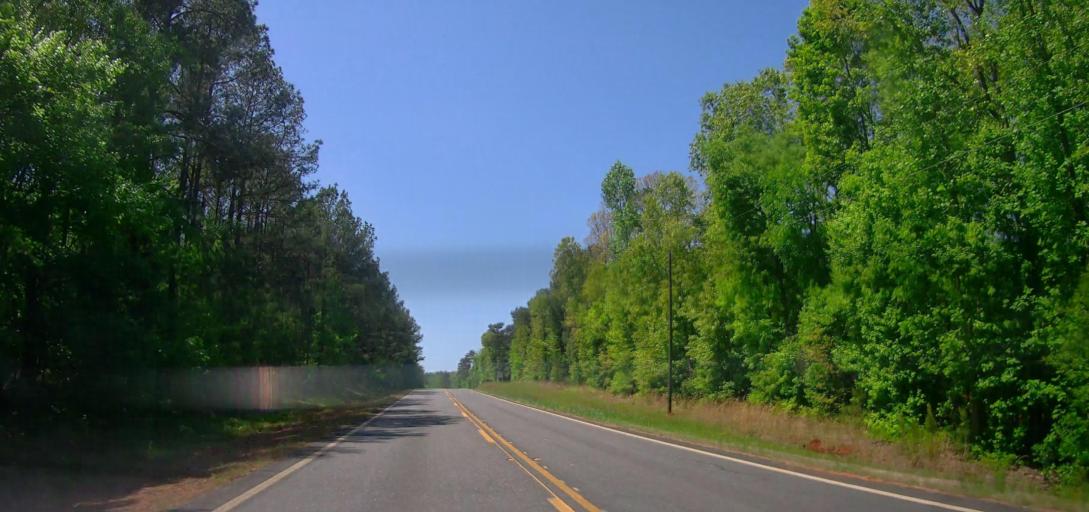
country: US
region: Georgia
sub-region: Putnam County
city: Eatonton
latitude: 33.2038
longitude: -83.4608
